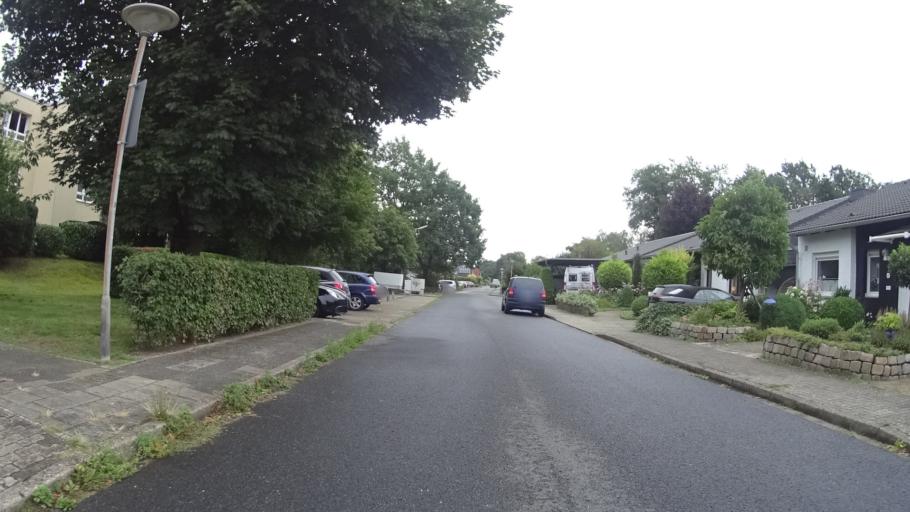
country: DE
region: Schleswig-Holstein
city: Henstedt-Ulzburg
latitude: 53.7694
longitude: 9.9735
